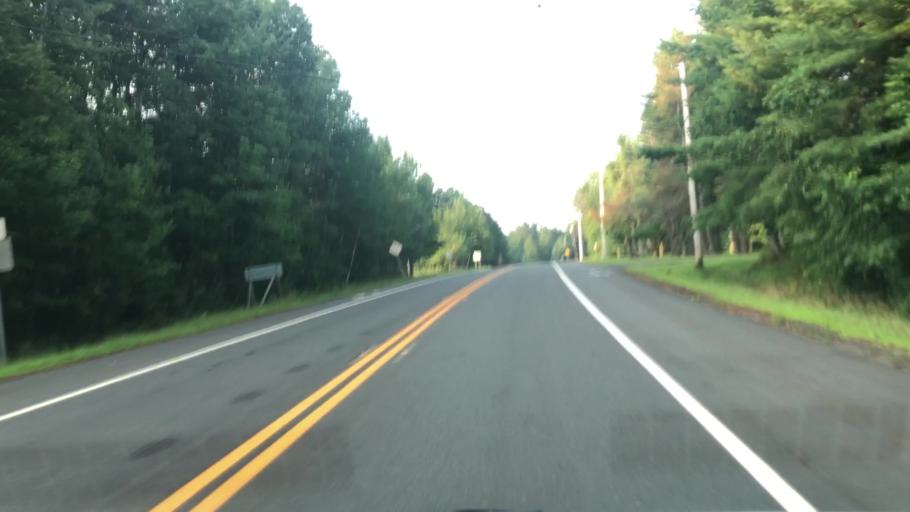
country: US
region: Massachusetts
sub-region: Franklin County
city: Ashfield
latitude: 42.5088
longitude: -72.8096
